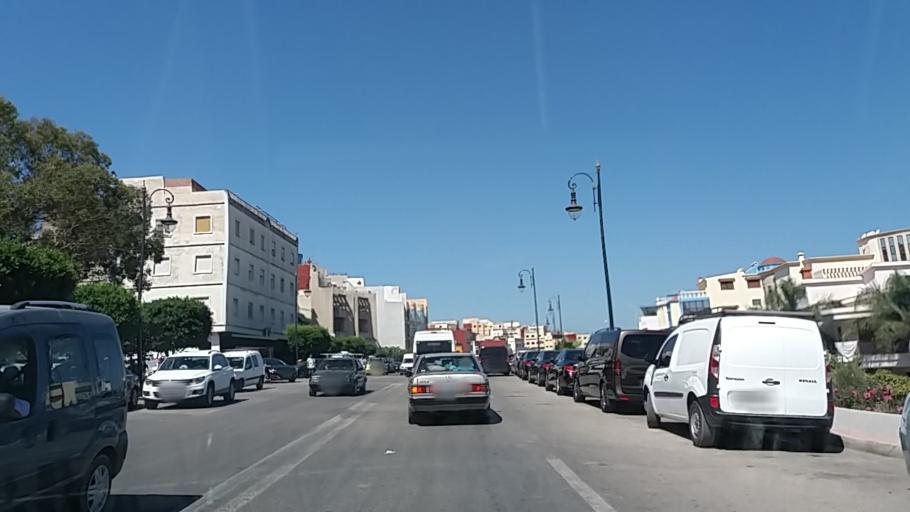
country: MA
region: Tanger-Tetouan
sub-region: Tanger-Assilah
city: Tangier
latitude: 35.7716
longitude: -5.7675
